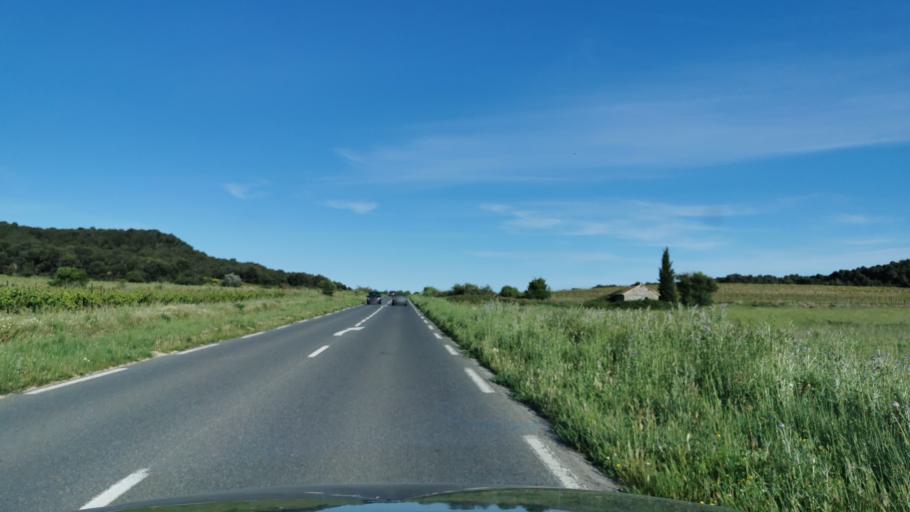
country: FR
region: Languedoc-Roussillon
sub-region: Departement de l'Aude
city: Moussan
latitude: 43.2109
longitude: 2.9434
